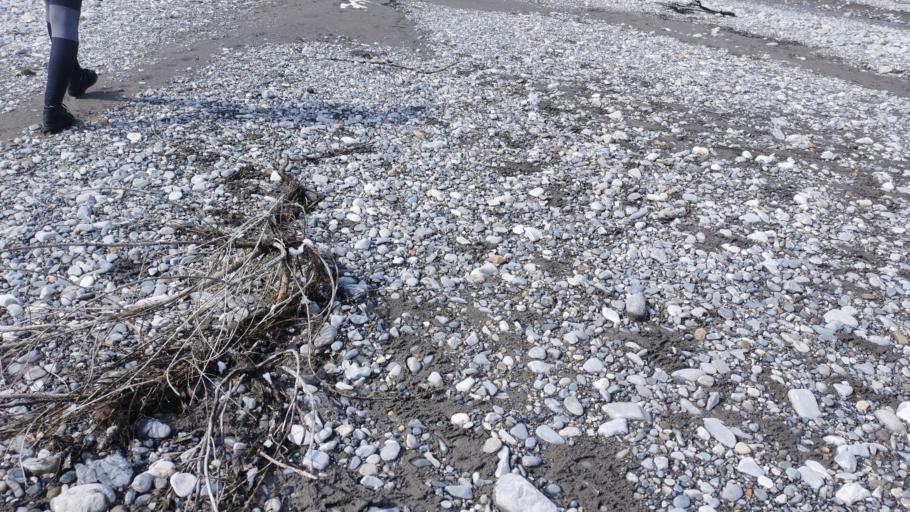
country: FR
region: Provence-Alpes-Cote d'Azur
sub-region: Departement des Alpes-de-Haute-Provence
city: Mallemoisson
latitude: 44.0628
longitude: 6.1718
